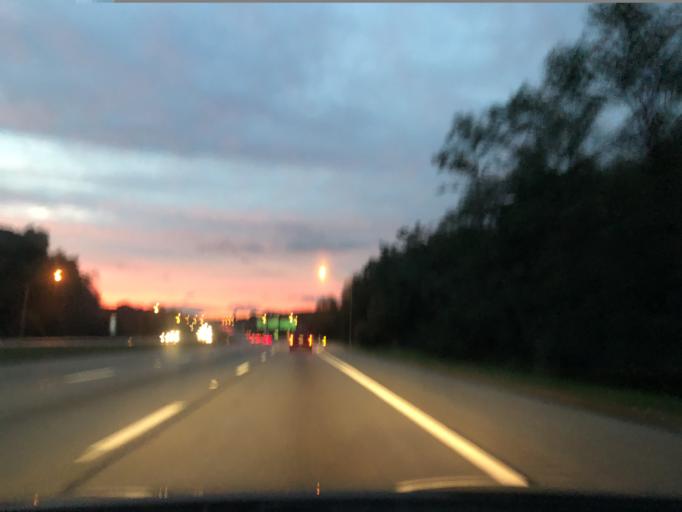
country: US
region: Ohio
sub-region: Hamilton County
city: The Village of Indian Hill
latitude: 39.2218
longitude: -84.2737
